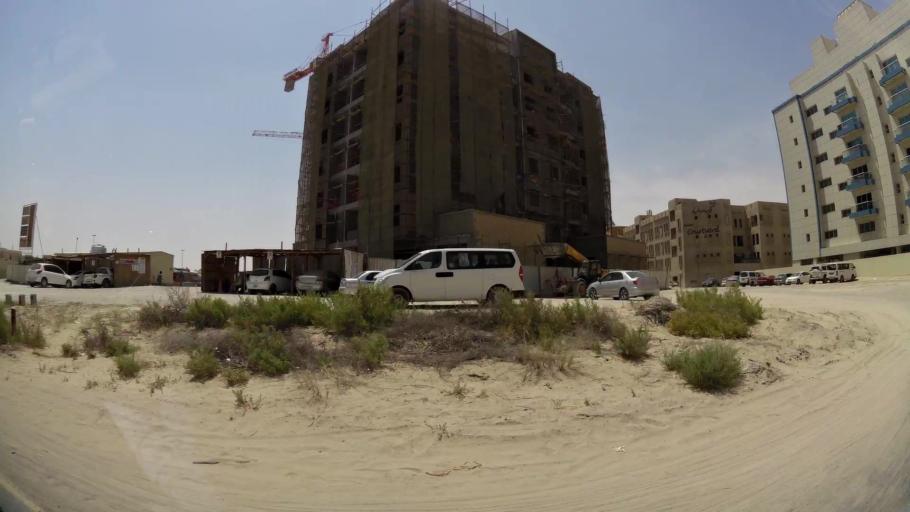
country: AE
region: Ash Shariqah
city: Sharjah
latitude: 25.1957
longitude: 55.4029
